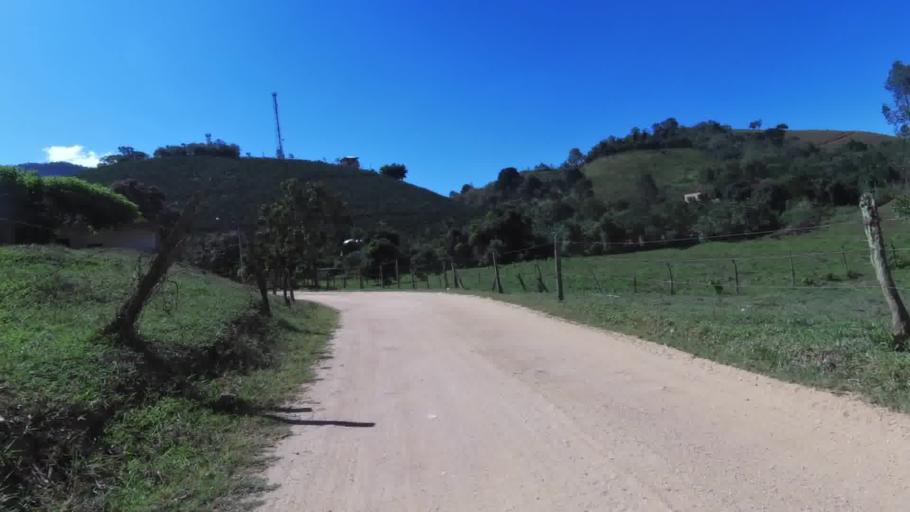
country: BR
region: Espirito Santo
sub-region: Rio Novo Do Sul
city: Rio Novo do Sul
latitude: -20.8712
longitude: -40.9336
